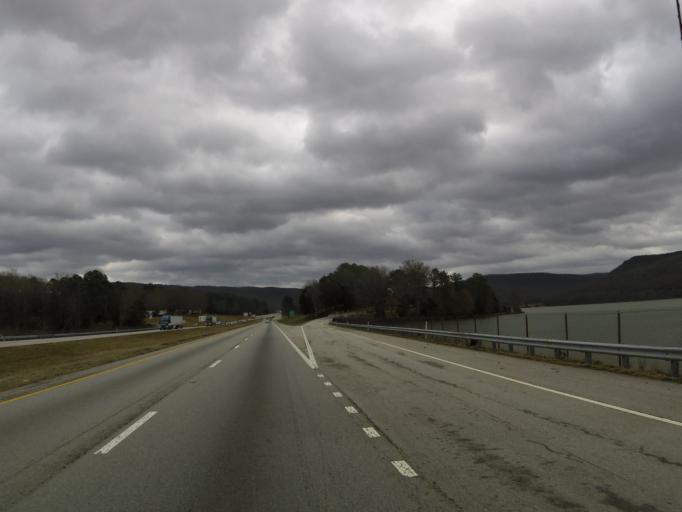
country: US
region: Tennessee
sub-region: Marion County
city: Jasper
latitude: 35.0265
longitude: -85.5629
